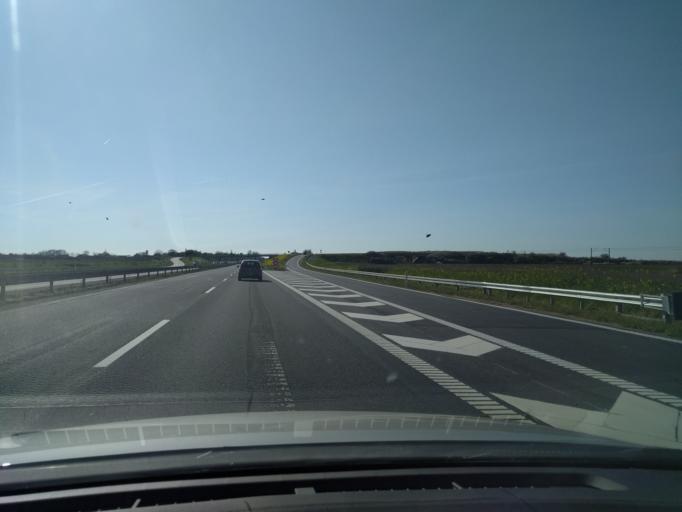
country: DK
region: Zealand
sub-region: Slagelse Kommune
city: Forlev
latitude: 55.3630
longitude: 11.2396
